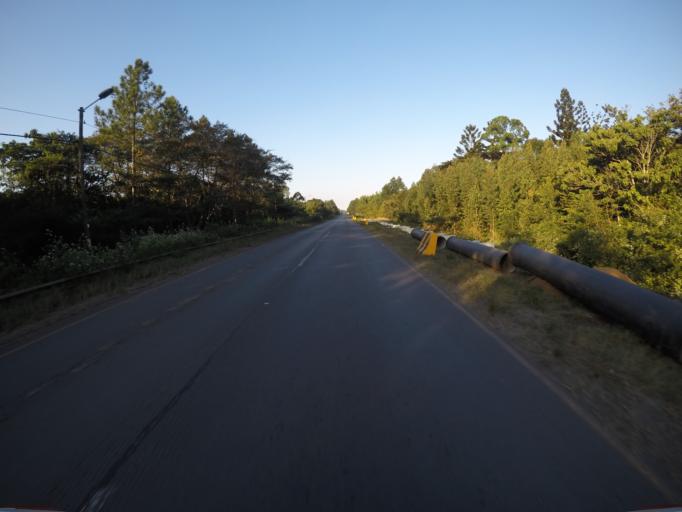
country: ZA
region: KwaZulu-Natal
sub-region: uThungulu District Municipality
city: KwaMbonambi
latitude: -28.6831
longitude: 32.1822
